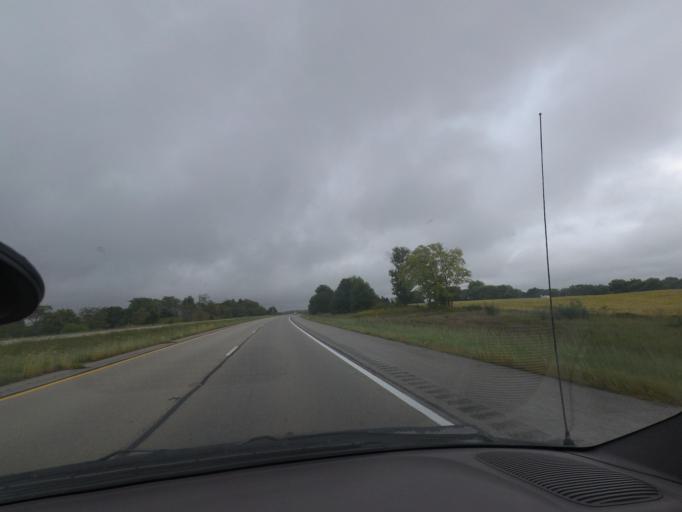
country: US
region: Illinois
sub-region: Piatt County
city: Monticello
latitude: 40.0892
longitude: -88.5191
